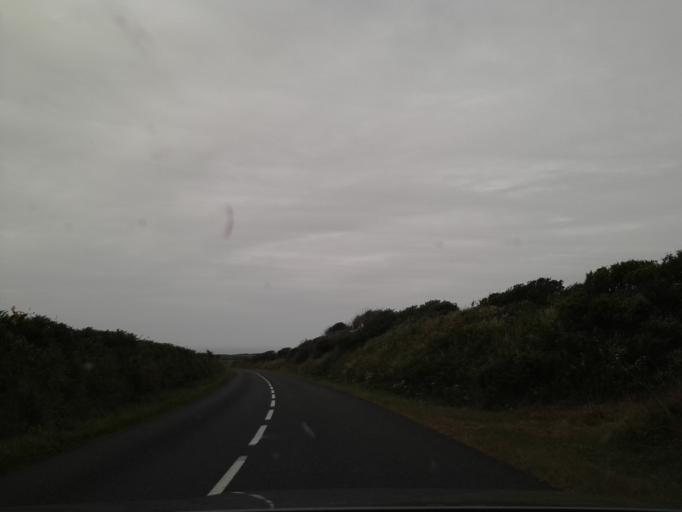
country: FR
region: Lower Normandy
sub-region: Departement de la Manche
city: Beaumont-Hague
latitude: 49.6994
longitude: -1.9262
